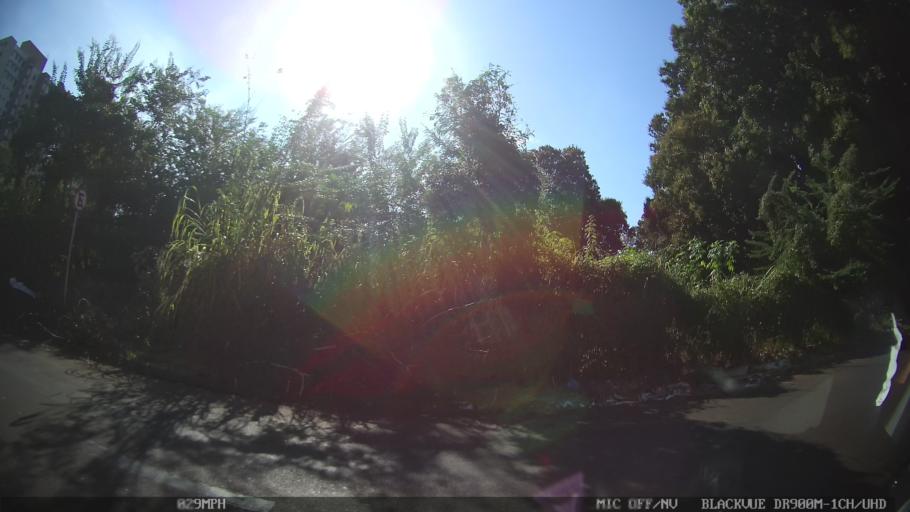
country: BR
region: Sao Paulo
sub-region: Ribeirao Preto
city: Ribeirao Preto
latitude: -21.1697
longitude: -47.7871
